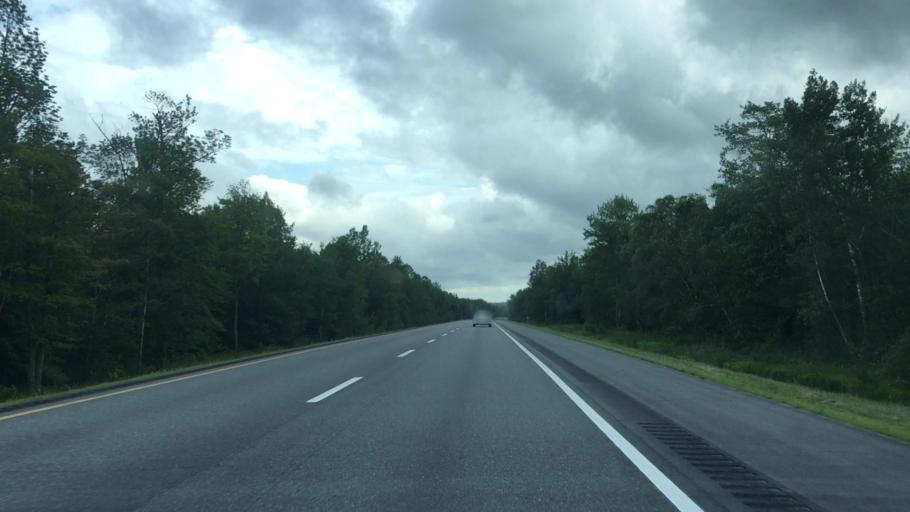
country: US
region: Maine
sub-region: Waldo County
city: Burnham
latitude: 44.7192
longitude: -69.4447
